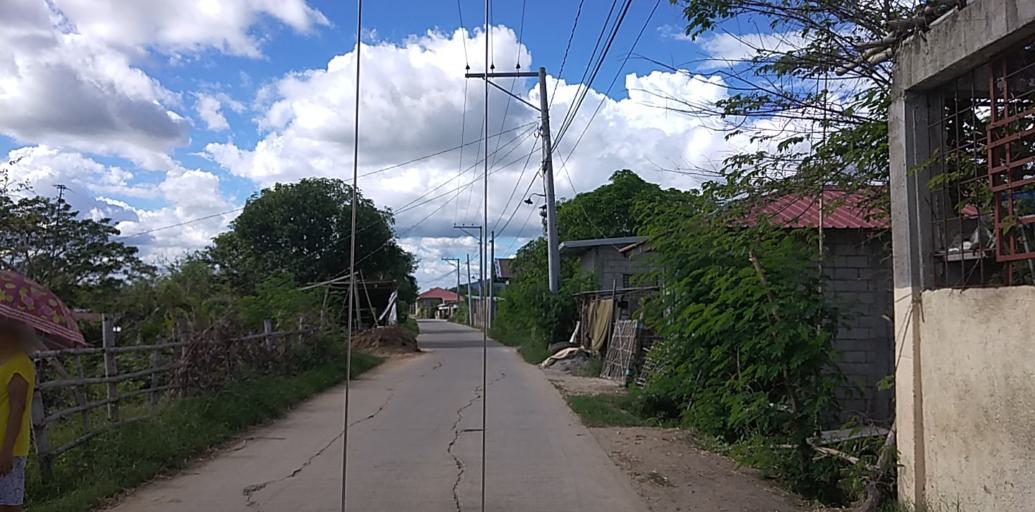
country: PH
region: Central Luzon
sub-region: Province of Pampanga
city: Candating
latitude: 15.1372
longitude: 120.8039
